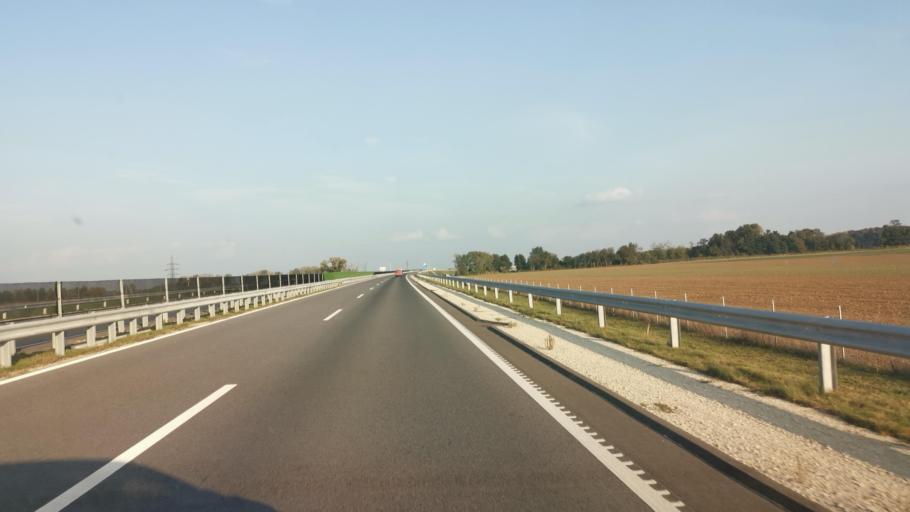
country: HU
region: Gyor-Moson-Sopron
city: Kapuvar
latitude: 47.5703
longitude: 17.0293
